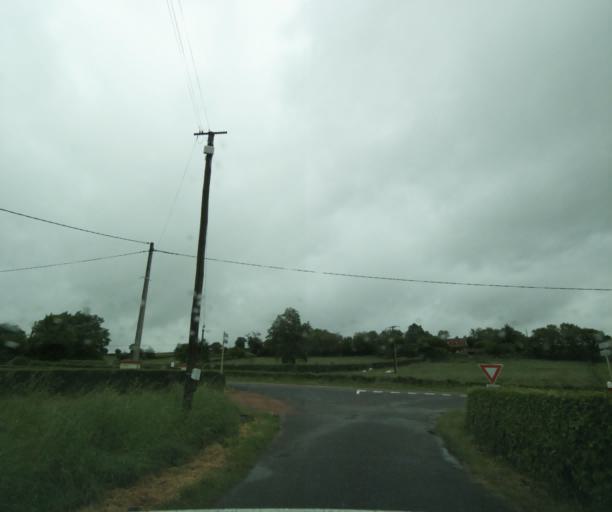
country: FR
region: Bourgogne
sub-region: Departement de Saone-et-Loire
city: Charolles
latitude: 46.4783
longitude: 4.4220
